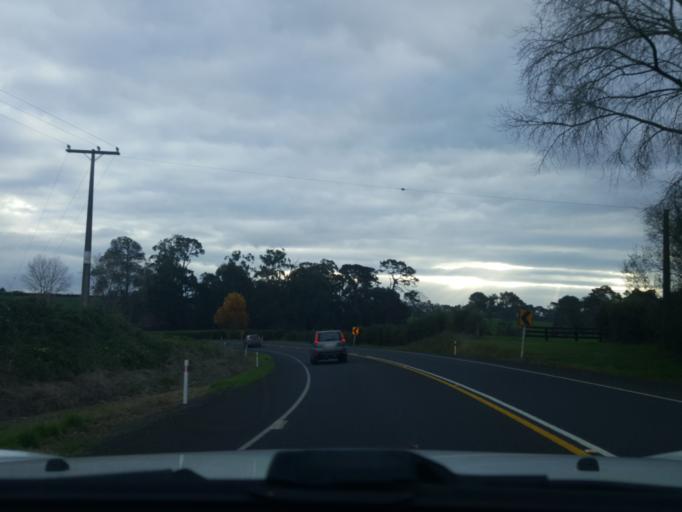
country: NZ
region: Waikato
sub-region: Matamata-Piako District
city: Matamata
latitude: -37.8762
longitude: 175.8184
